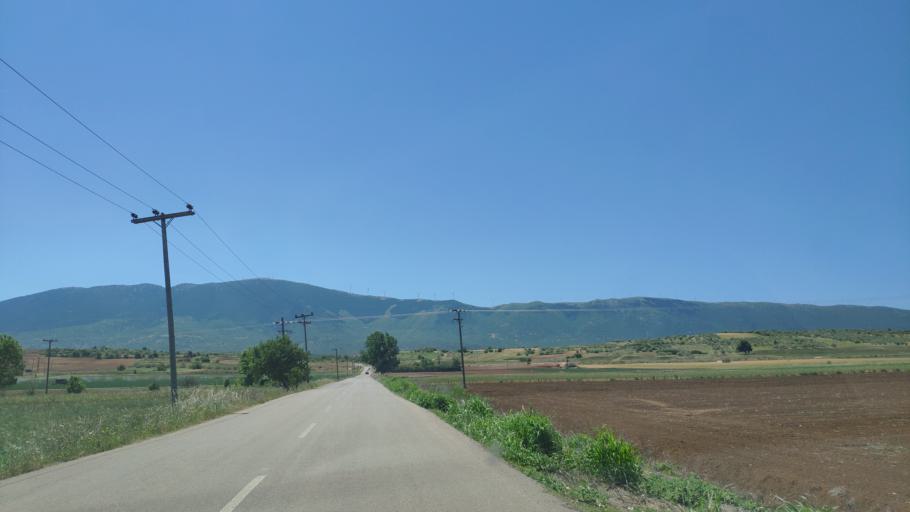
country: GR
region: Central Greece
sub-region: Nomos Voiotias
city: Kaparellion
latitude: 38.2575
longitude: 23.2352
